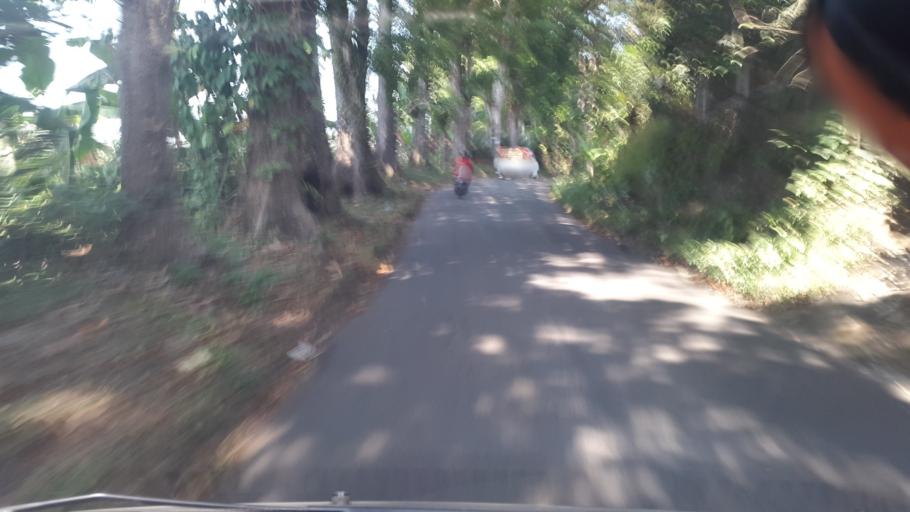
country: ID
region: West Java
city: Cicurug
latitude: -6.8465
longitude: 106.6977
